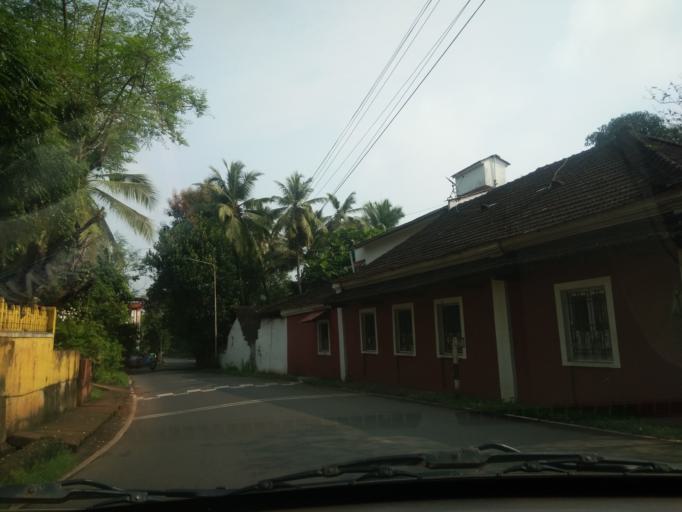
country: IN
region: Goa
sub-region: South Goa
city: Madgaon
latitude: 15.2836
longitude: 73.9640
